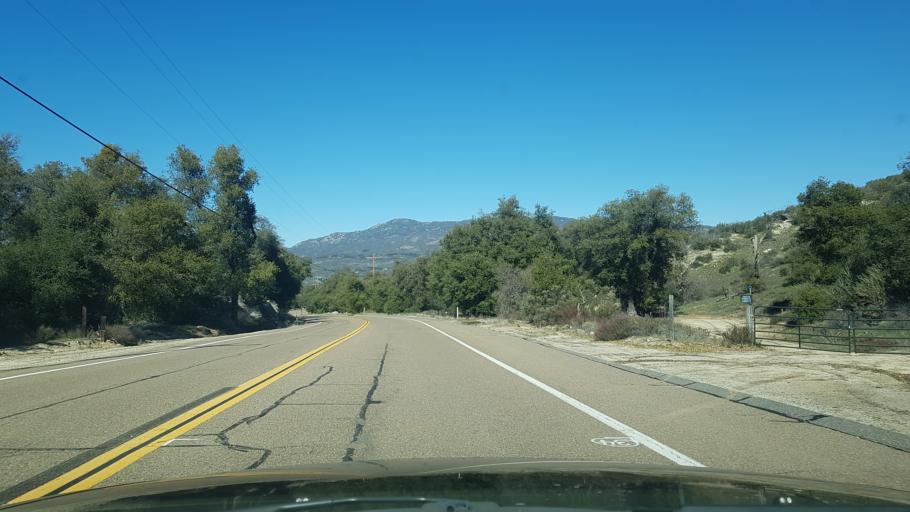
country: US
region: California
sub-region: San Diego County
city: Julian
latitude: 33.2092
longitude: -116.6032
